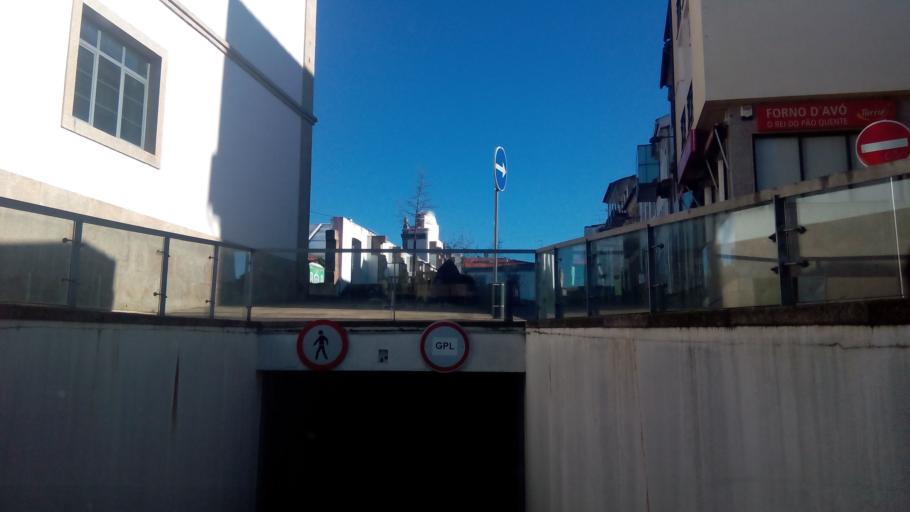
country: PT
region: Braganca
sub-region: Braganca Municipality
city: Braganca
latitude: 41.8051
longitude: -6.7569
